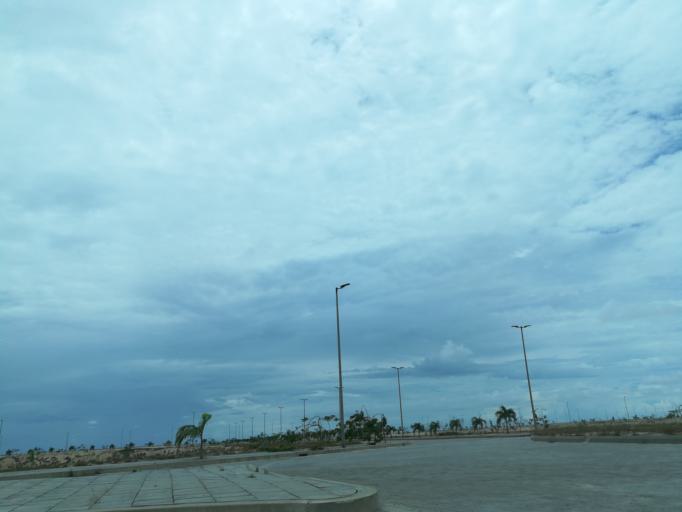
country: NG
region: Lagos
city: Ikoyi
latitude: 6.4081
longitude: 3.4169
